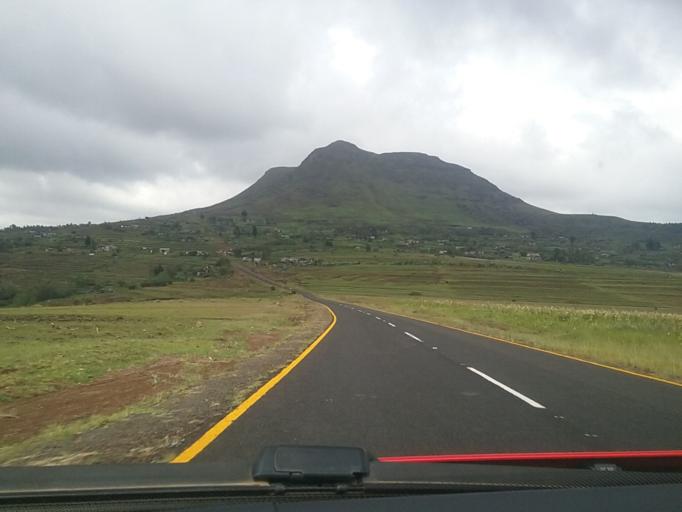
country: LS
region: Berea
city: Teyateyaneng
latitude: -29.2462
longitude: 27.8511
